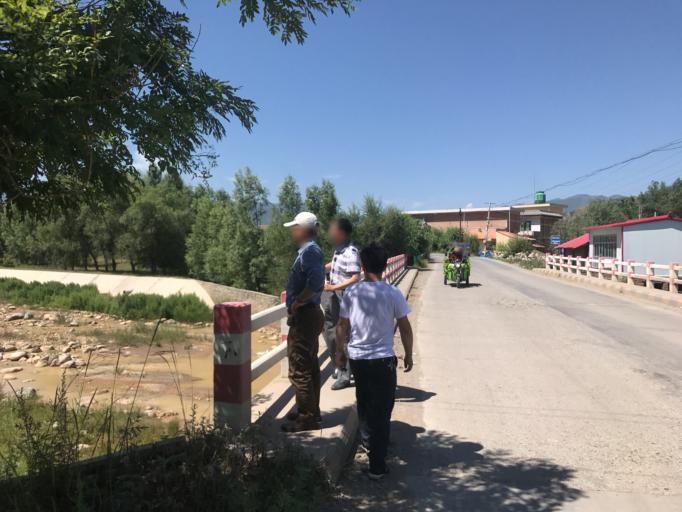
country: CN
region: Gansu Sheng
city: Hanji
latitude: 35.4758
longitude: 103.0450
